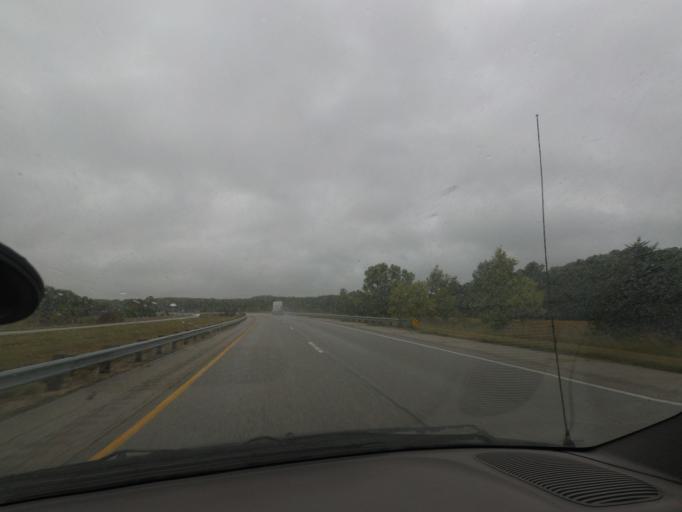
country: US
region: Illinois
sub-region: Pike County
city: Barry
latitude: 39.7163
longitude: -91.1073
